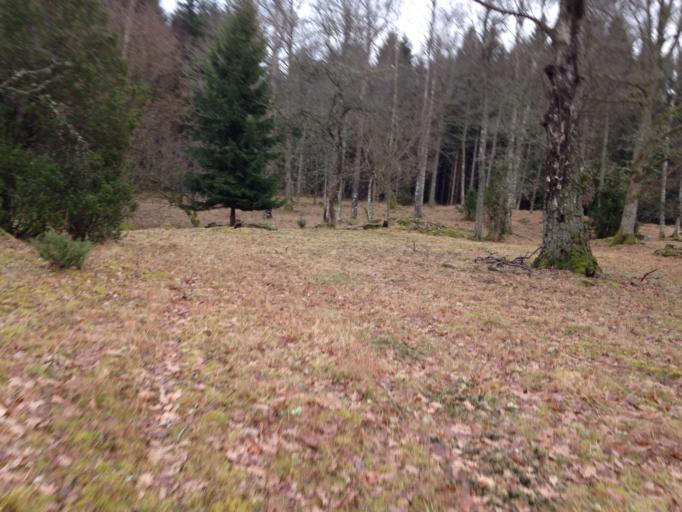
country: SE
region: Joenkoeping
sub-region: Varnamo Kommun
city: Bor
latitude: 57.0341
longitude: 14.1830
